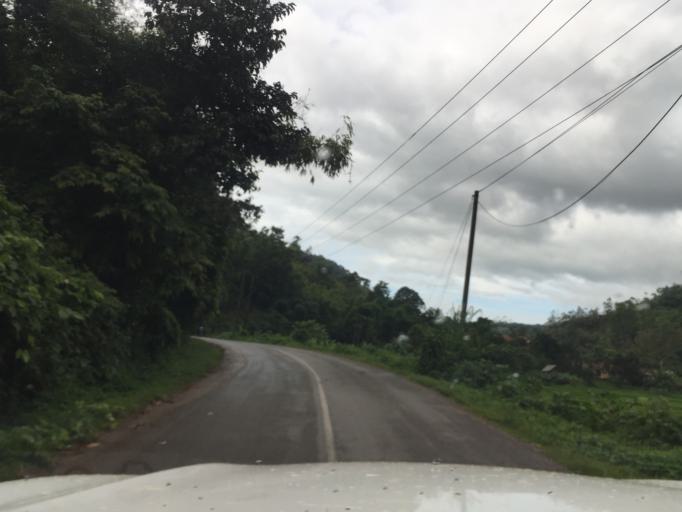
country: LA
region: Oudomxai
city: Muang La
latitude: 20.8171
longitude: 102.0930
